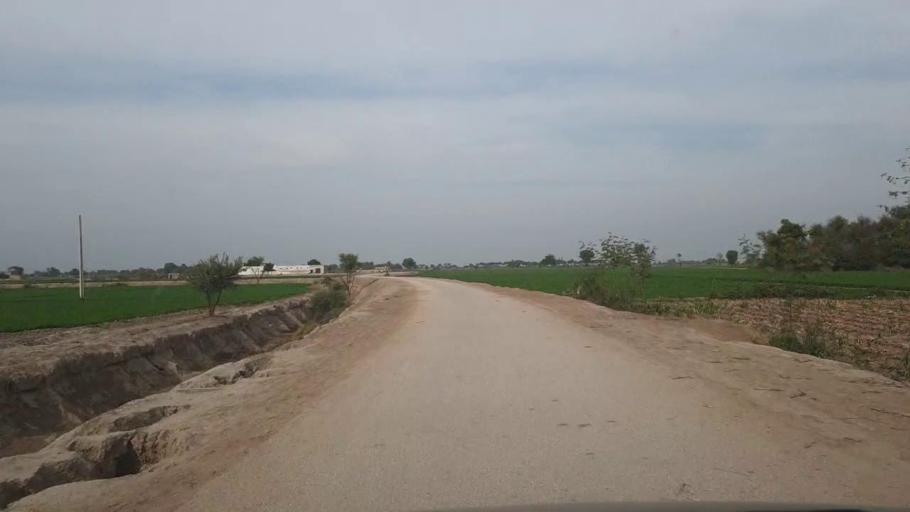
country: PK
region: Sindh
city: Shahpur Chakar
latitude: 26.1184
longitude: 68.5234
